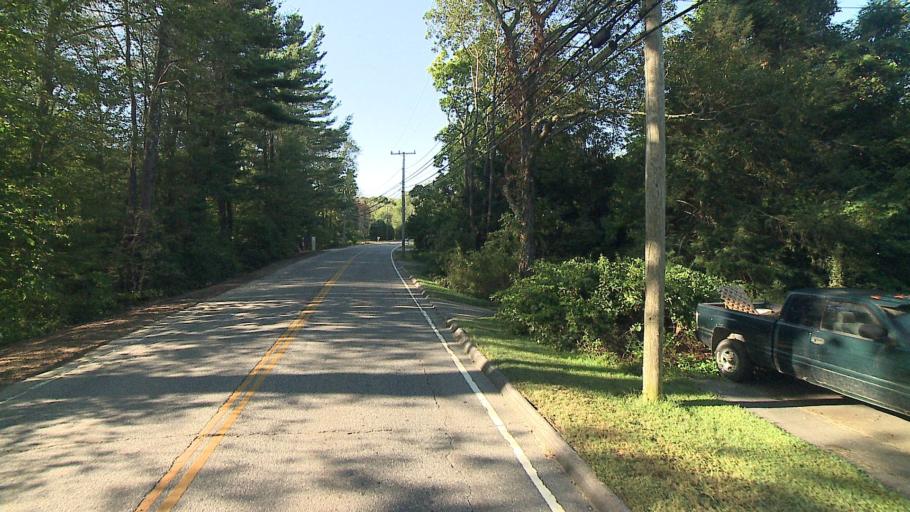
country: US
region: Connecticut
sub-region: Windham County
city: Plainfield Village
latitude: 41.6528
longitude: -71.9305
